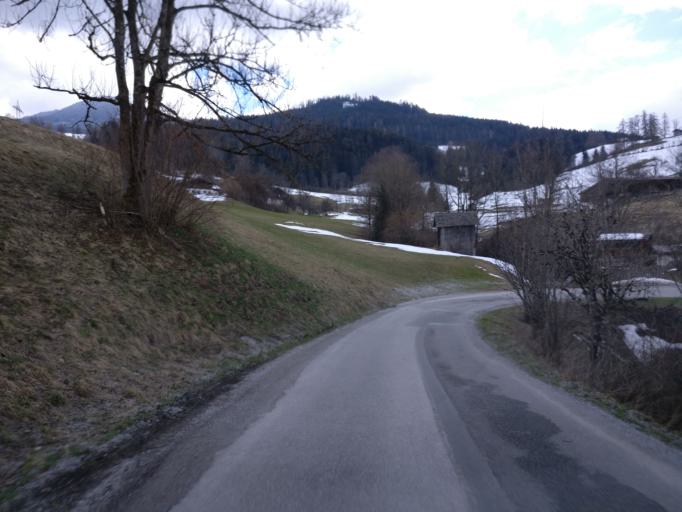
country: AT
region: Salzburg
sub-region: Politischer Bezirk Sankt Johann im Pongau
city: Bischofshofen
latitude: 47.4213
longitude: 13.2346
